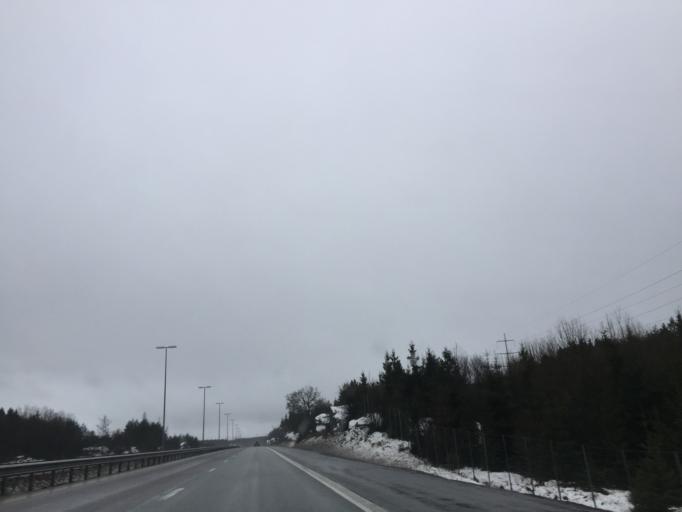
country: NO
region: Akershus
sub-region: Vestby
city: Vestby
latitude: 59.5516
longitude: 10.7224
